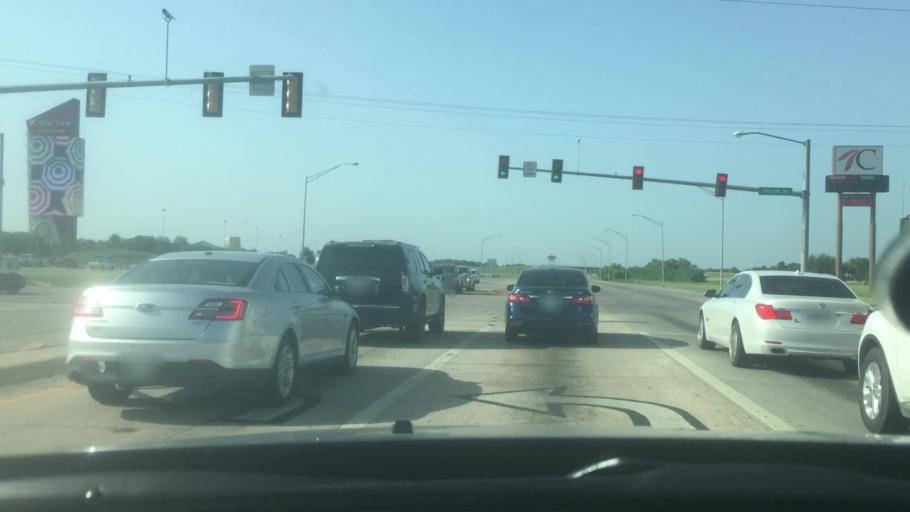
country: US
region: Oklahoma
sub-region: Bryan County
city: Calera
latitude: 33.9546
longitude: -96.4167
